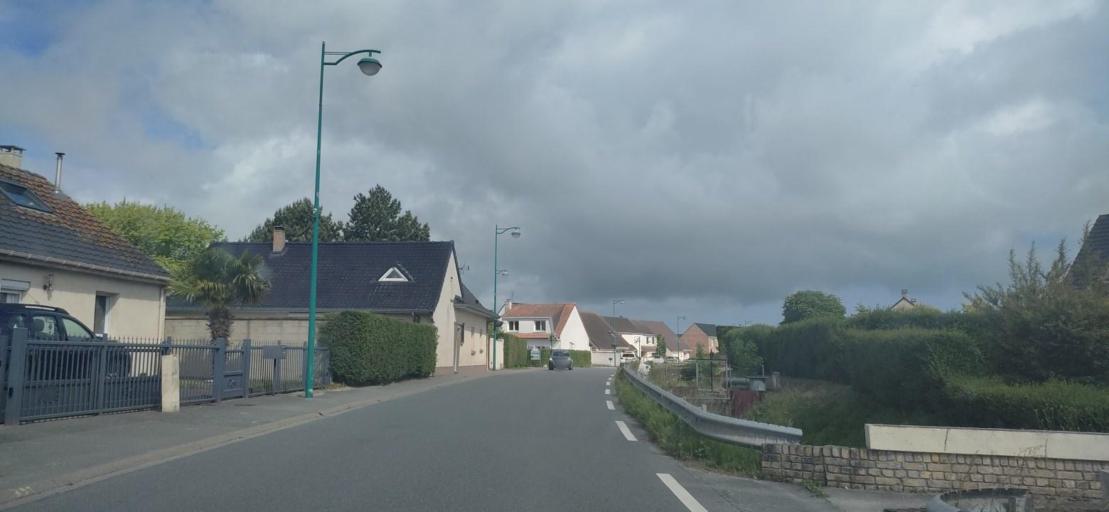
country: FR
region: Nord-Pas-de-Calais
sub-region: Departement du Pas-de-Calais
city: Oye-Plage
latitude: 50.9809
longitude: 2.0377
